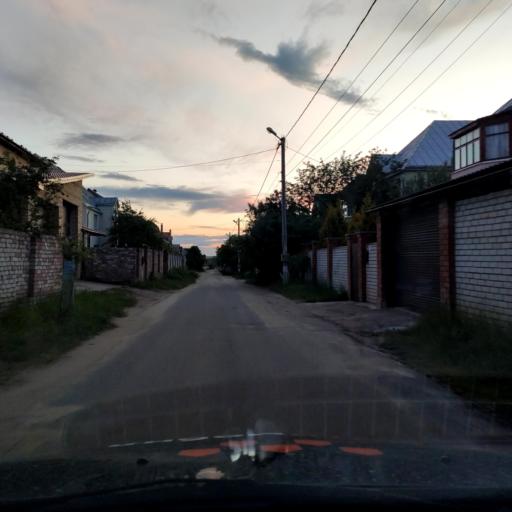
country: RU
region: Voronezj
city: Podgornoye
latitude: 51.7468
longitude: 39.1558
